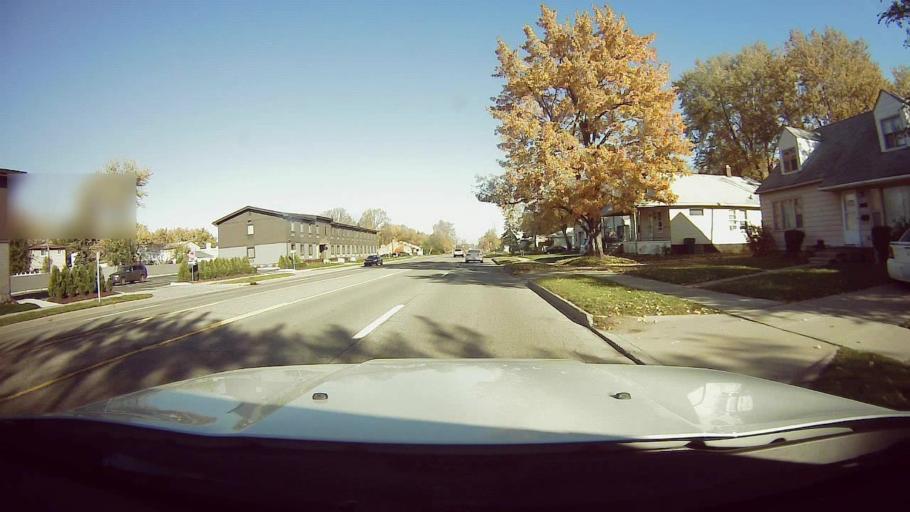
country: US
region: Michigan
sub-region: Oakland County
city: Berkley
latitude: 42.5072
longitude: -83.2032
